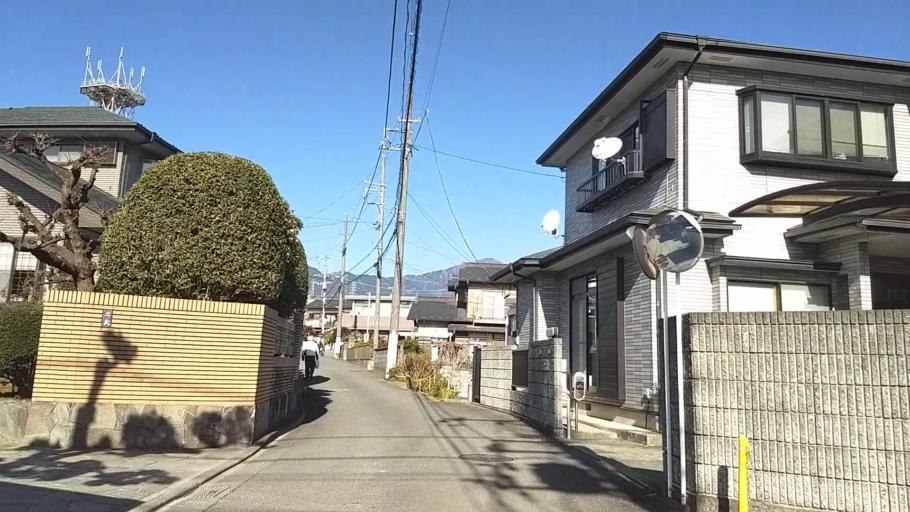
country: JP
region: Kanagawa
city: Hadano
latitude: 35.3753
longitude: 139.2312
